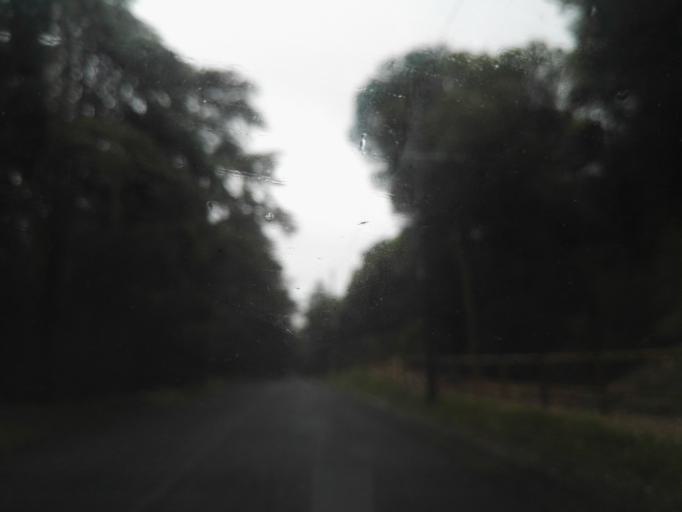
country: PT
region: Lisbon
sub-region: Odivelas
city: Pontinha
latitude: 38.7309
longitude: -9.1791
